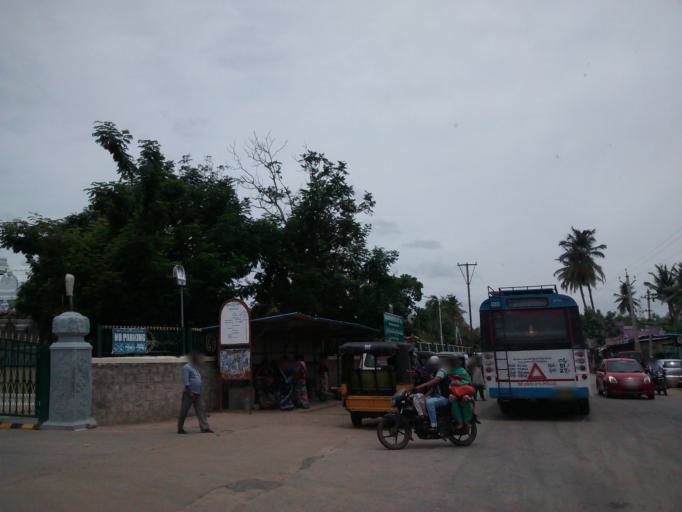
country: IN
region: Andhra Pradesh
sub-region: Chittoor
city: Narasingapuram
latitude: 13.6110
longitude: 79.3291
